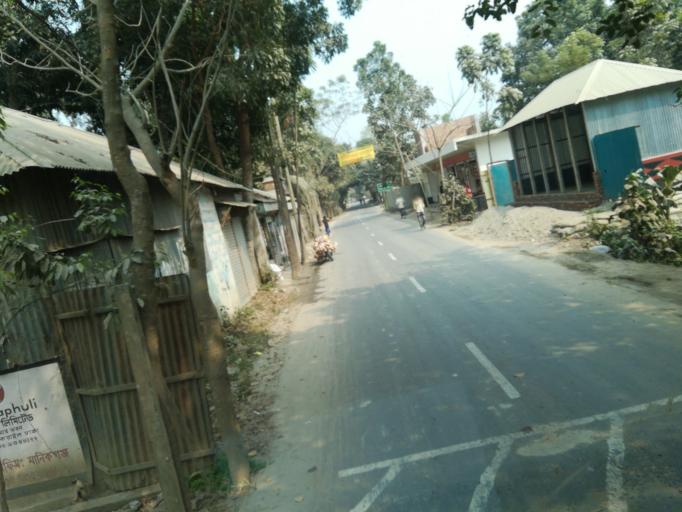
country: BD
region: Dhaka
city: Nagarpur
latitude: 23.9736
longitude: 89.8395
